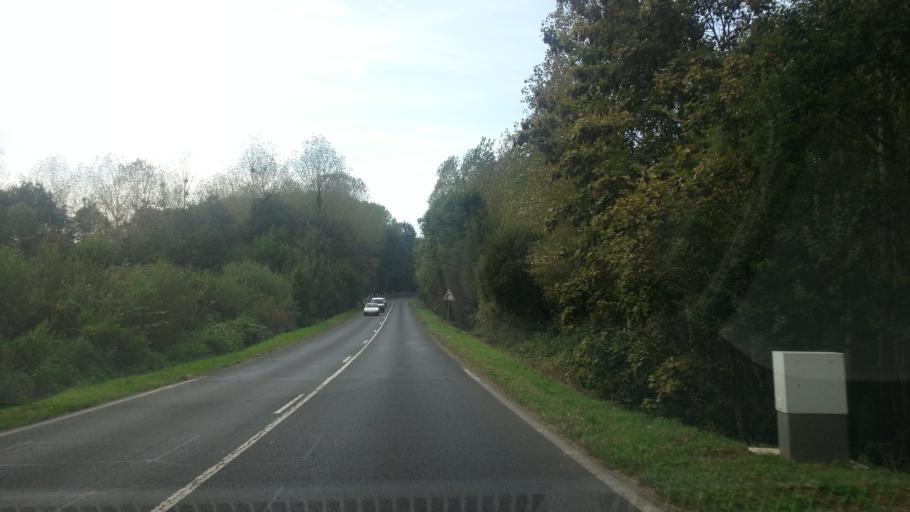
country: FR
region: Picardie
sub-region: Departement de l'Oise
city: Senlis
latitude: 49.2087
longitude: 2.5666
